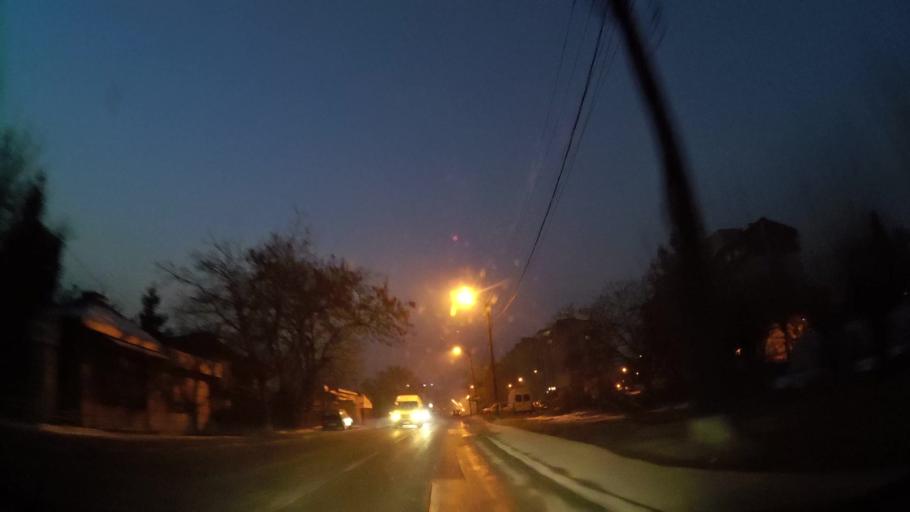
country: MK
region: Kisela Voda
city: Kisela Voda
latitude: 41.9967
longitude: 21.4969
